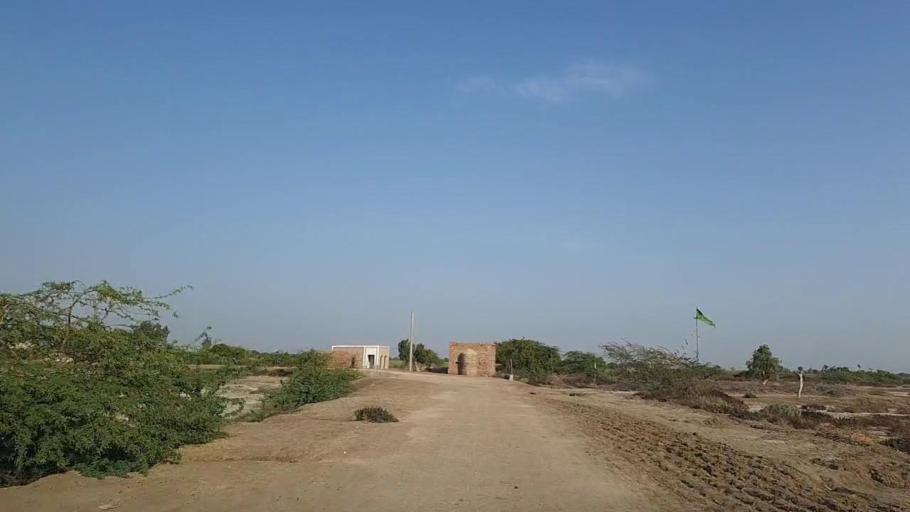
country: PK
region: Sindh
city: Dhoro Naro
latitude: 25.4277
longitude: 69.4851
